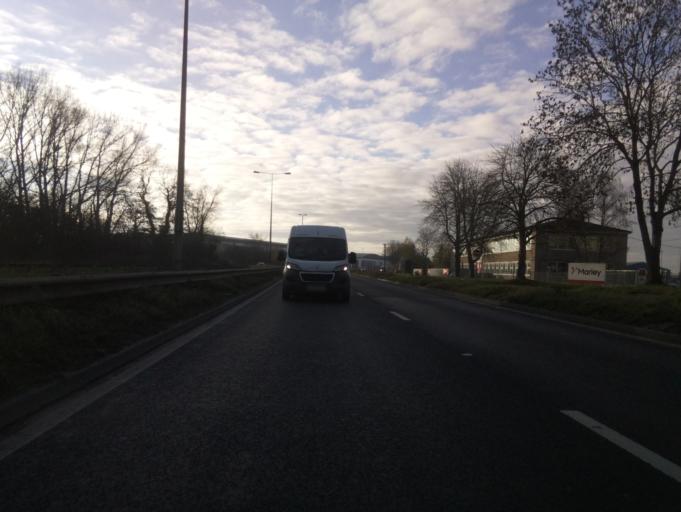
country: GB
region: England
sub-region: Staffordshire
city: Barton under Needwood
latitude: 52.7794
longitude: -1.6821
